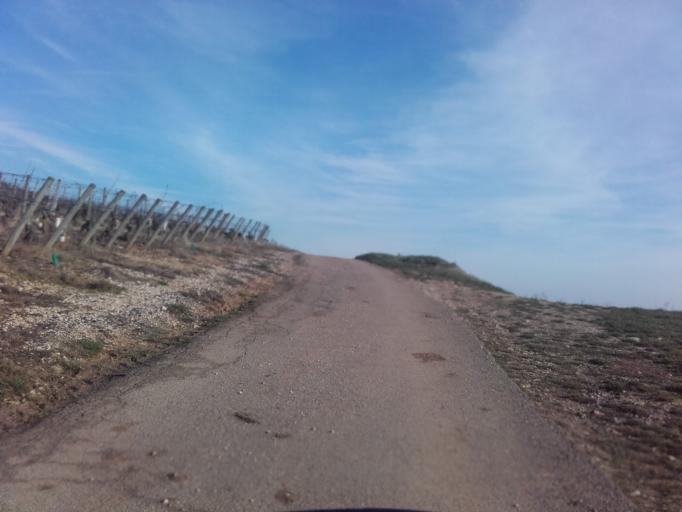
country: FR
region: Bourgogne
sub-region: Departement de Saone-et-Loire
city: Chagny
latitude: 46.9199
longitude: 4.7071
